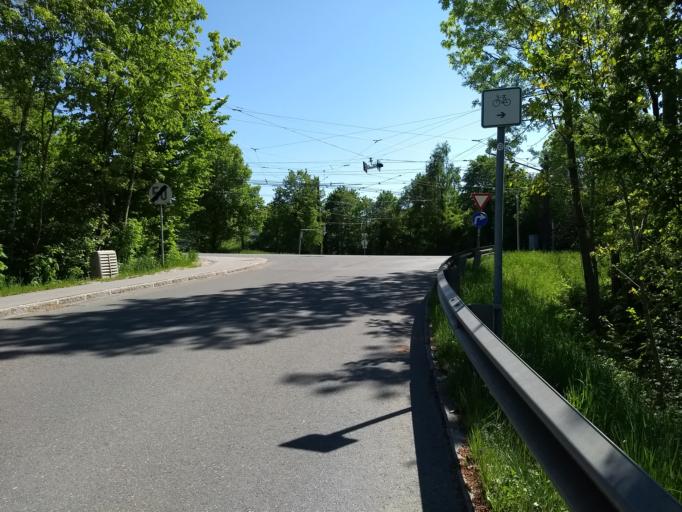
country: AT
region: Salzburg
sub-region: Politischer Bezirk Salzburg-Umgebung
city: Elsbethen
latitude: 47.7711
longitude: 13.0769
